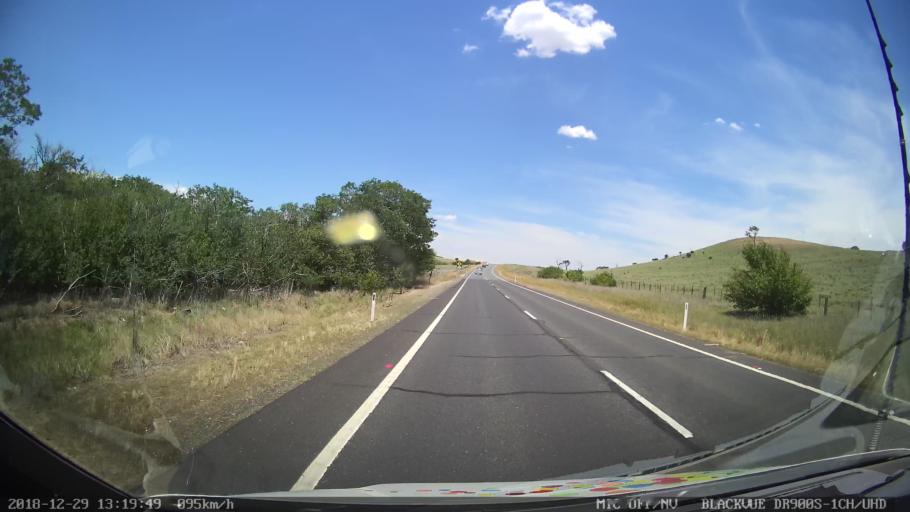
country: AU
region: Australian Capital Territory
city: Macarthur
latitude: -35.7705
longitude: 149.1617
